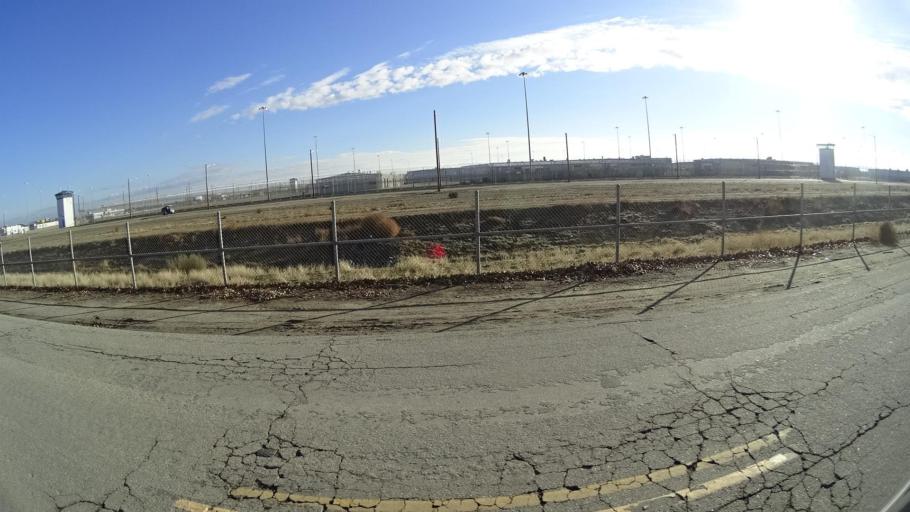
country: US
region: California
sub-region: Kern County
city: Delano
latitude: 35.7692
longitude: -119.3298
